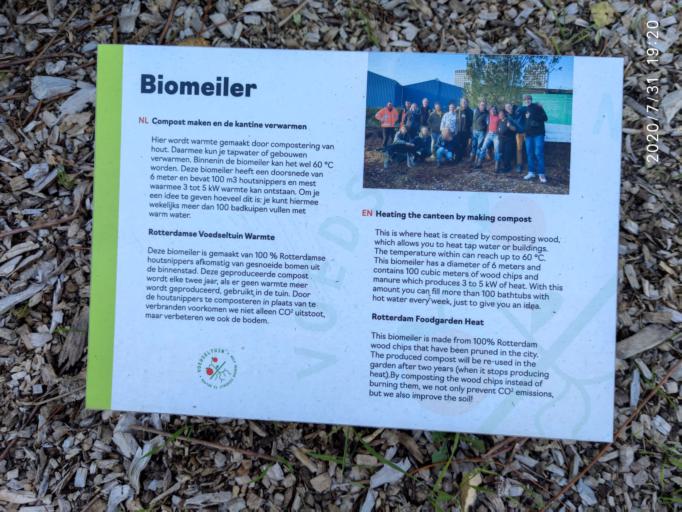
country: NL
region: South Holland
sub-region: Gemeente Rotterdam
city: Delfshaven
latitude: 51.9088
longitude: 4.4328
